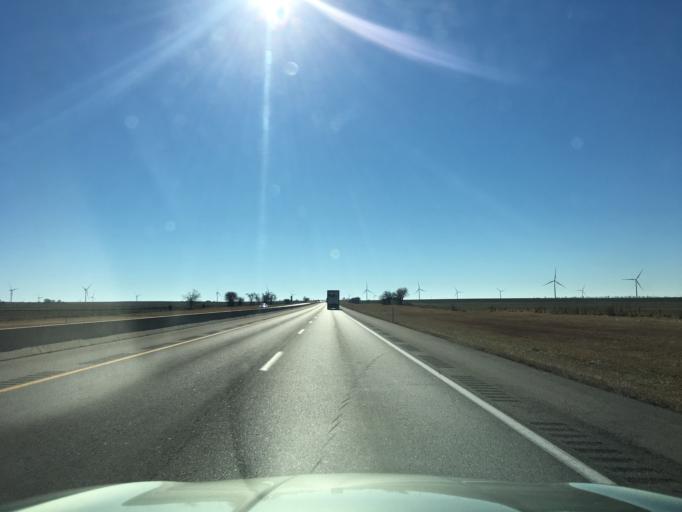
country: US
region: Kansas
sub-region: Sumner County
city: Wellington
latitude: 37.1768
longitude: -97.3396
